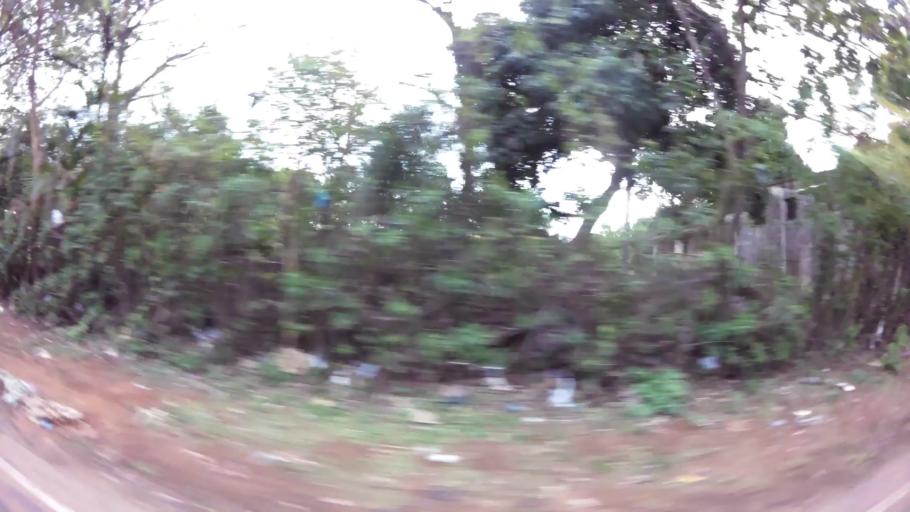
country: PY
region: Central
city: Villa Elisa
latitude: -25.3458
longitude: -57.5608
